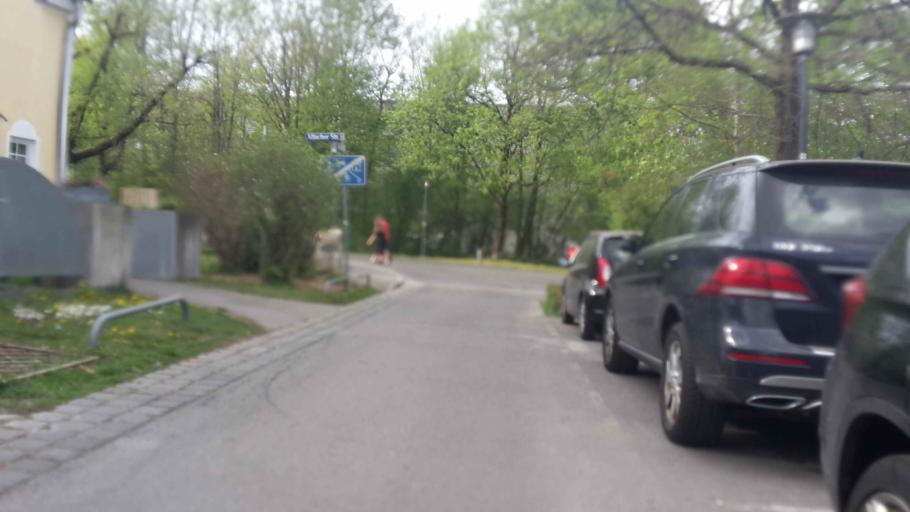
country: DE
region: Bavaria
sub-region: Upper Bavaria
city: Karlsfeld
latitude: 48.1822
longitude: 11.4703
